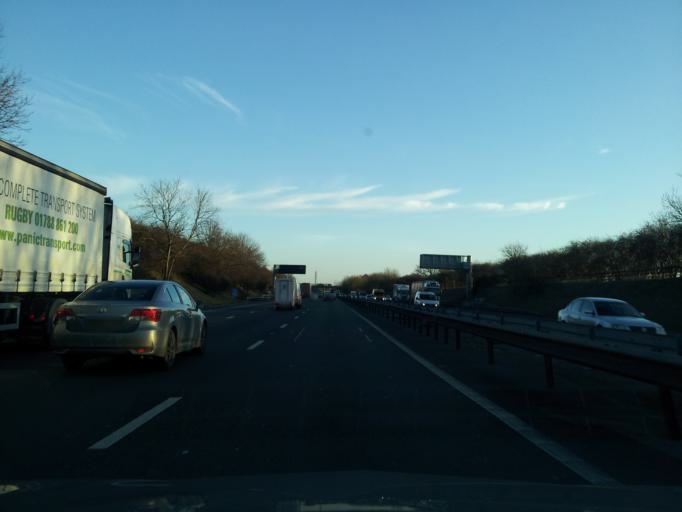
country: GB
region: England
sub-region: Milton Keynes
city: Gayhurst
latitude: 52.0888
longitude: -0.7542
